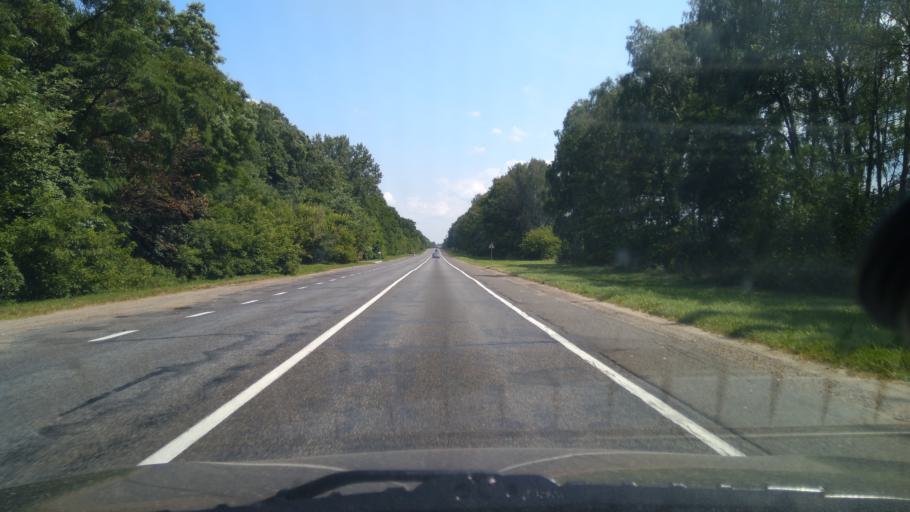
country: BY
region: Brest
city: Baranovichi
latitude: 53.1191
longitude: 26.1296
